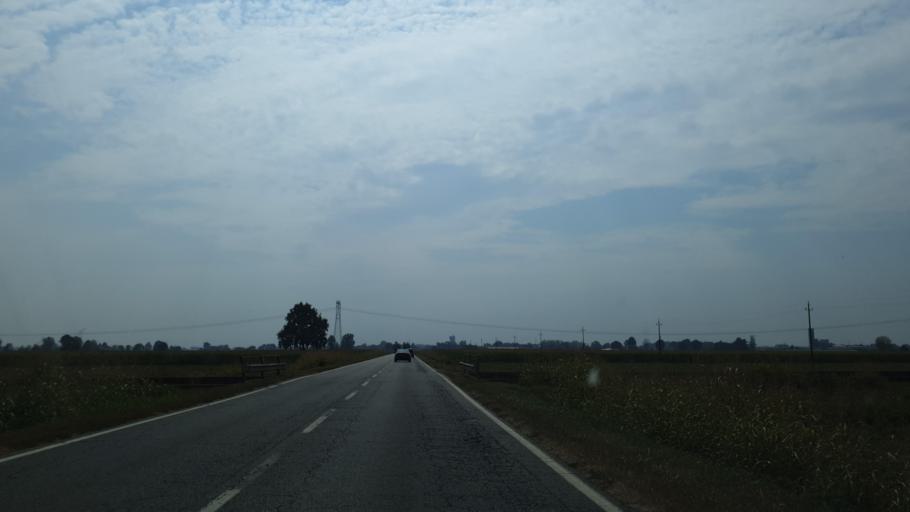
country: IT
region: Lombardy
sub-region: Provincia di Cremona
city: Pieve San Giacomo
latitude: 45.1153
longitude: 10.1881
